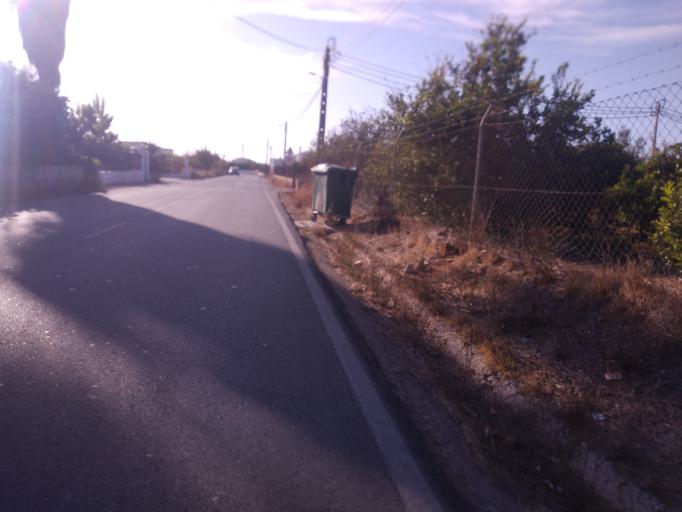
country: PT
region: Faro
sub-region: Faro
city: Faro
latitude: 37.0514
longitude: -7.9349
